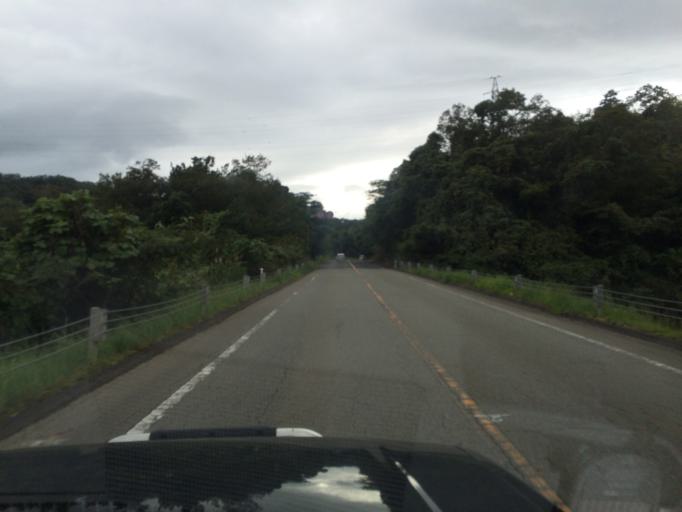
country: JP
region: Hyogo
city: Toyooka
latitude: 35.5082
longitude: 134.8001
